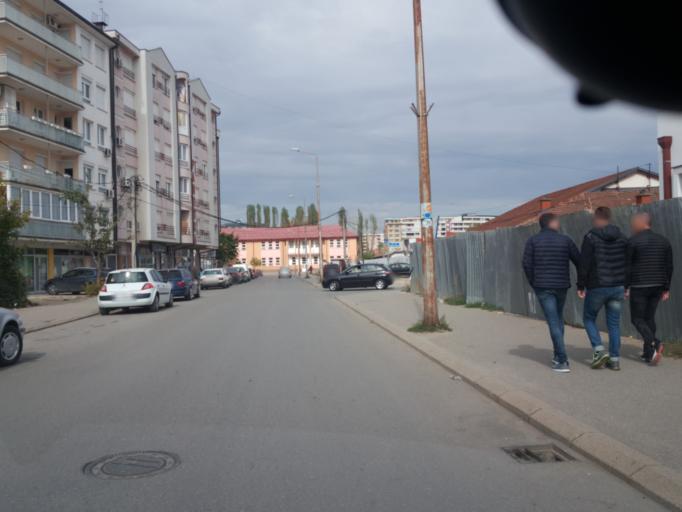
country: XK
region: Gjakova
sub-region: Komuna e Gjakoves
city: Gjakove
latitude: 42.3830
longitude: 20.4344
